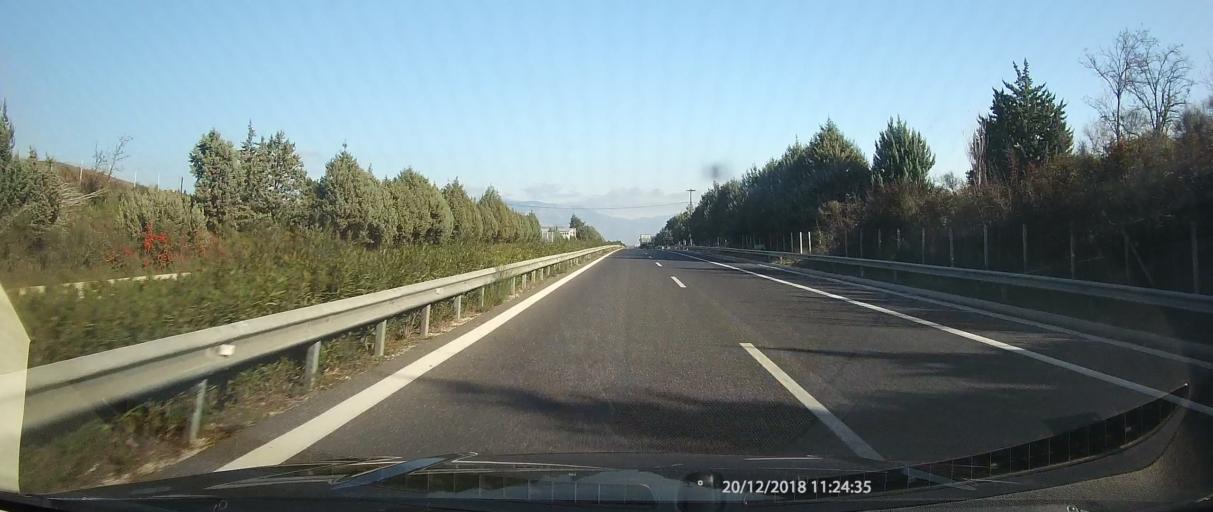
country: GR
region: Peloponnese
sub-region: Nomos Korinthias
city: Arkhaia Korinthos
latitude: 37.8809
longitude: 22.8867
